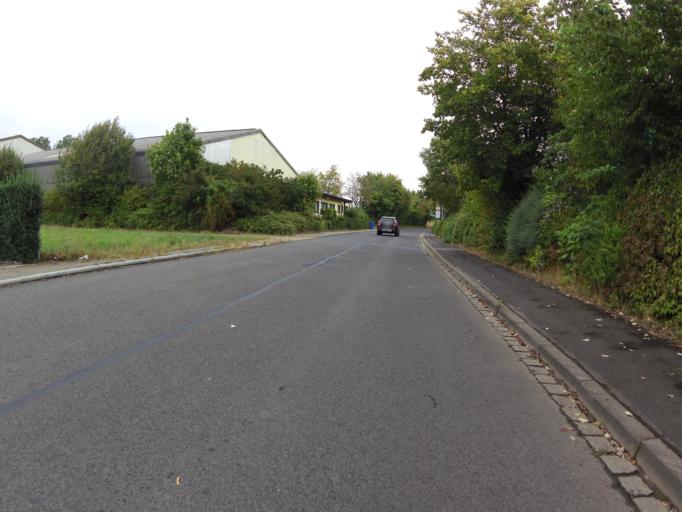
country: DE
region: Bavaria
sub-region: Regierungsbezirk Unterfranken
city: Guntersleben
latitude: 49.8745
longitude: 9.9073
